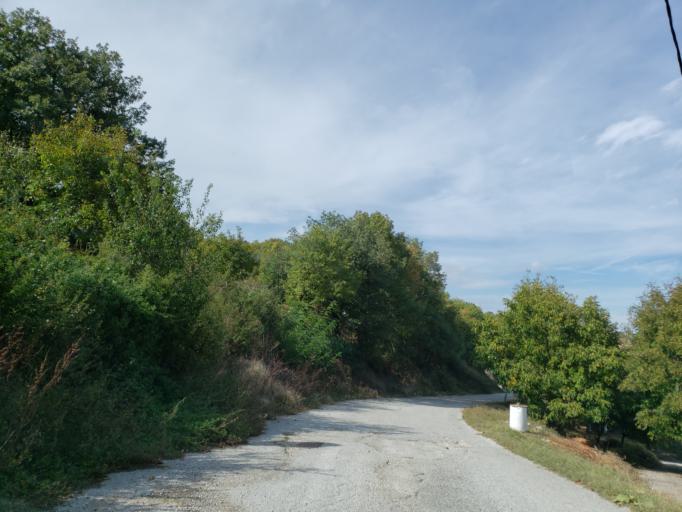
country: GR
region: Thessaly
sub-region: Trikala
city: Kastraki
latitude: 39.7712
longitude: 21.6621
